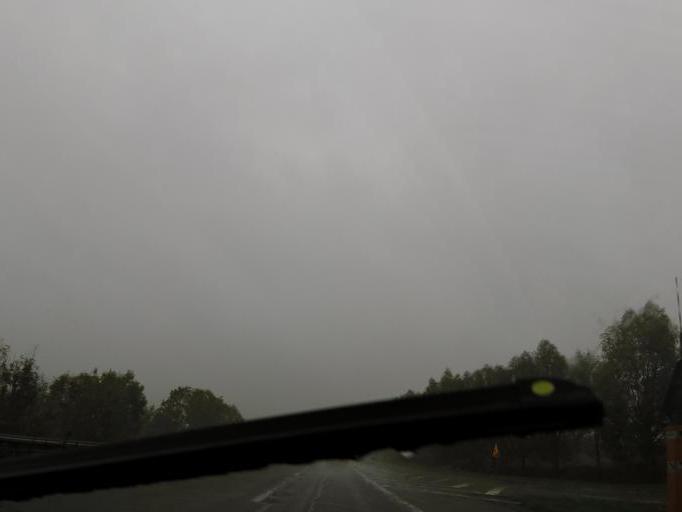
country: FR
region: Picardie
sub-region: Departement de l'Aisne
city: Essomes-sur-Marne
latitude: 49.0556
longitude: 3.3215
